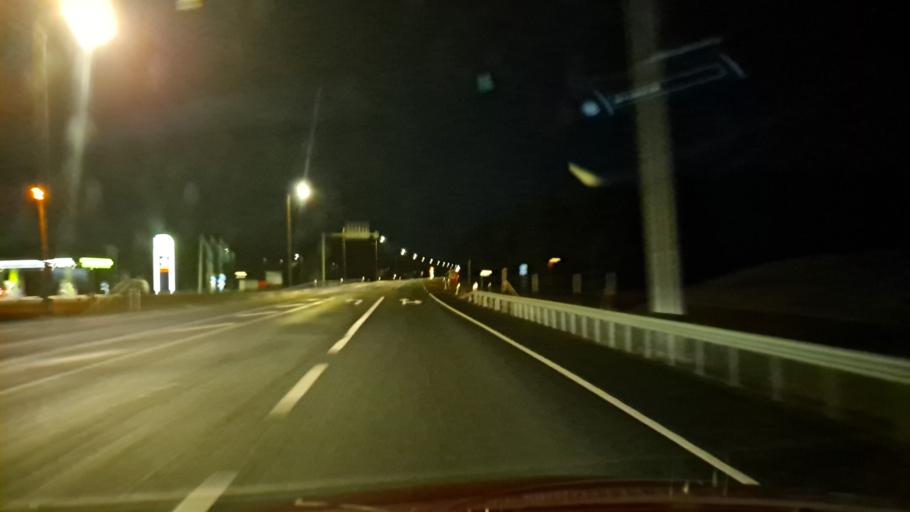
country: FI
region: Northern Ostrobothnia
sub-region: Oulunkaari
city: Kuivaniemi
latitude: 65.5852
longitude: 25.1976
